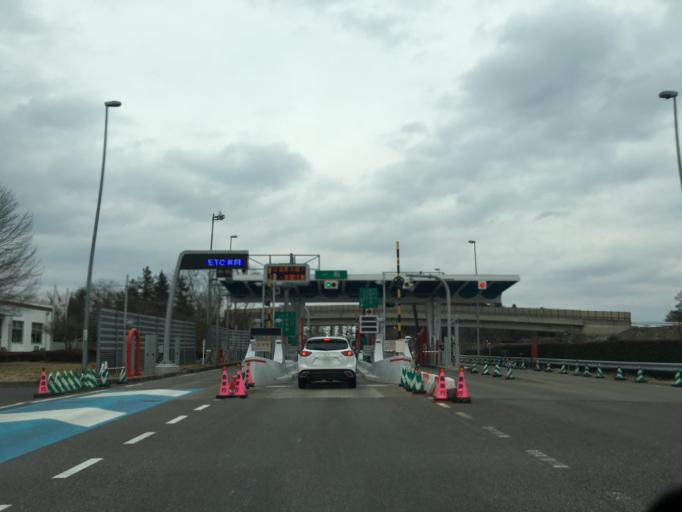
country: JP
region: Fukushima
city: Koriyama
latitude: 37.3645
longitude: 140.3143
